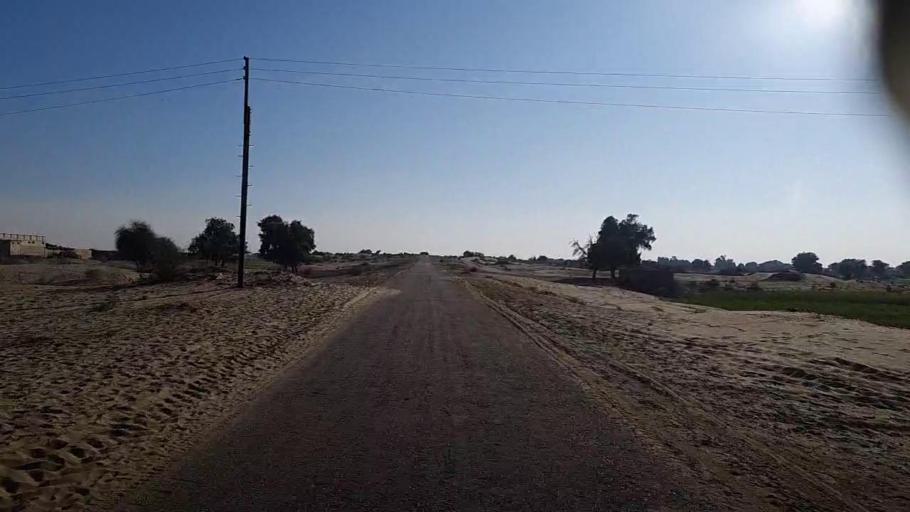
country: PK
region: Sindh
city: Khairpur
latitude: 27.9045
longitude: 69.7495
